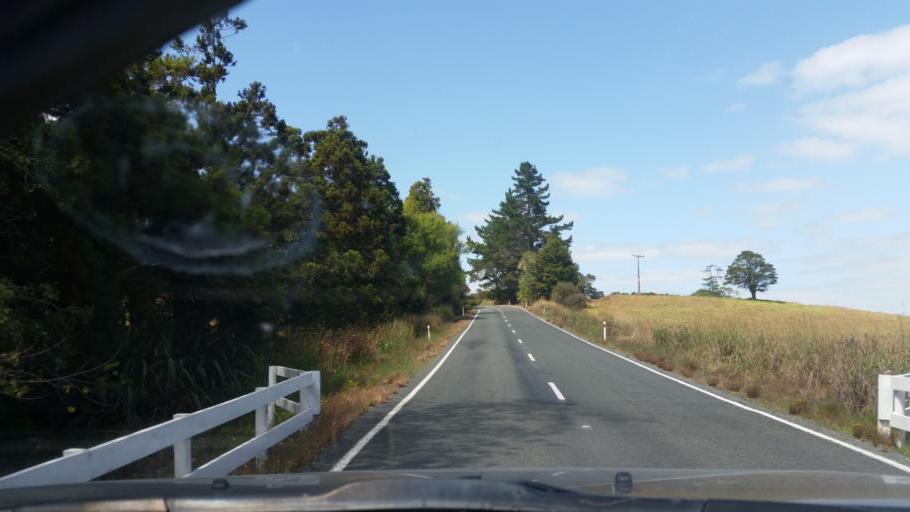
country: NZ
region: Northland
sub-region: Whangarei
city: Ruakaka
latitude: -35.9884
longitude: 174.2931
